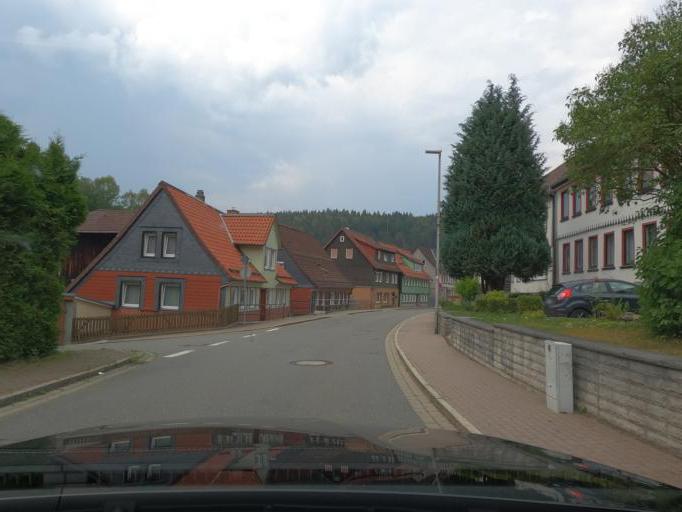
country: DE
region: Lower Saxony
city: Wildemann
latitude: 51.8671
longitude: 10.2891
